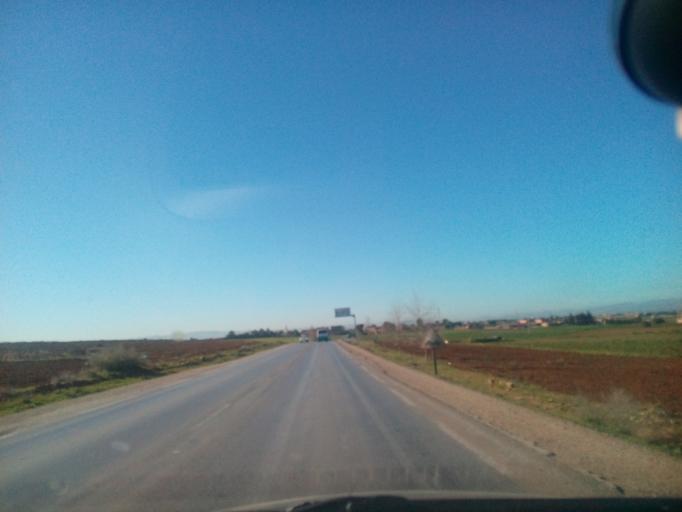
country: DZ
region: Relizane
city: Djidiouia
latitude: 35.8919
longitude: 0.7309
